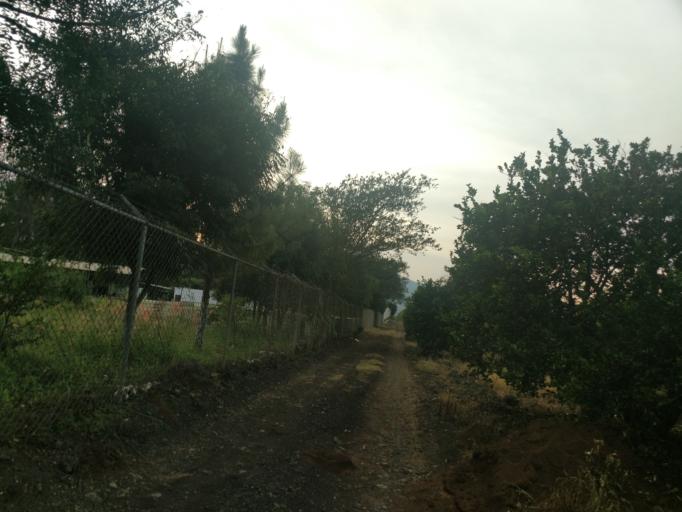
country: MX
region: Nayarit
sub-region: Tepic
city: La Corregidora
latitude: 21.4641
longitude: -104.8068
